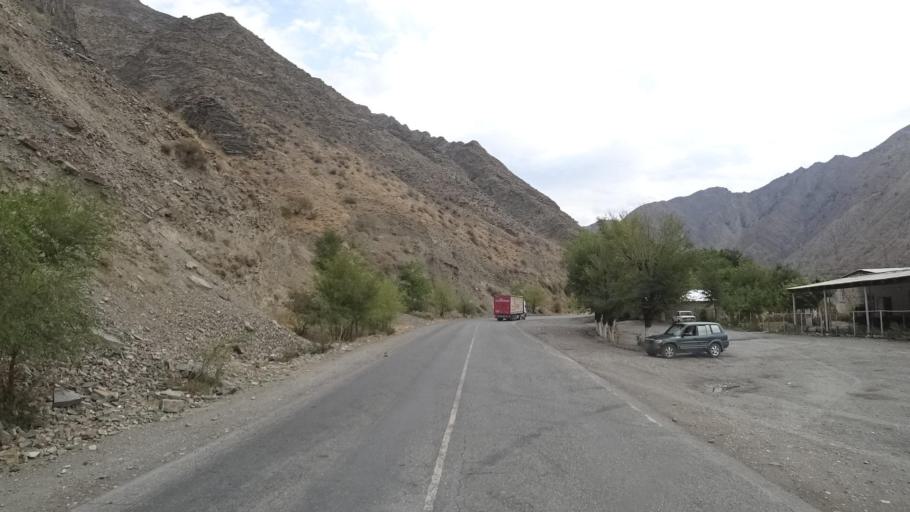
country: KG
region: Jalal-Abad
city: Tash-Kumyr
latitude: 41.4979
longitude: 72.3478
